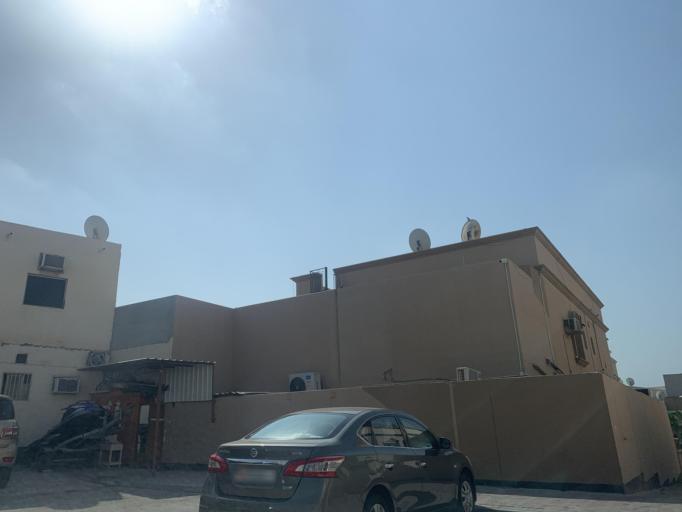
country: BH
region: Central Governorate
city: Madinat Hamad
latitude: 26.1233
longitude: 50.5042
